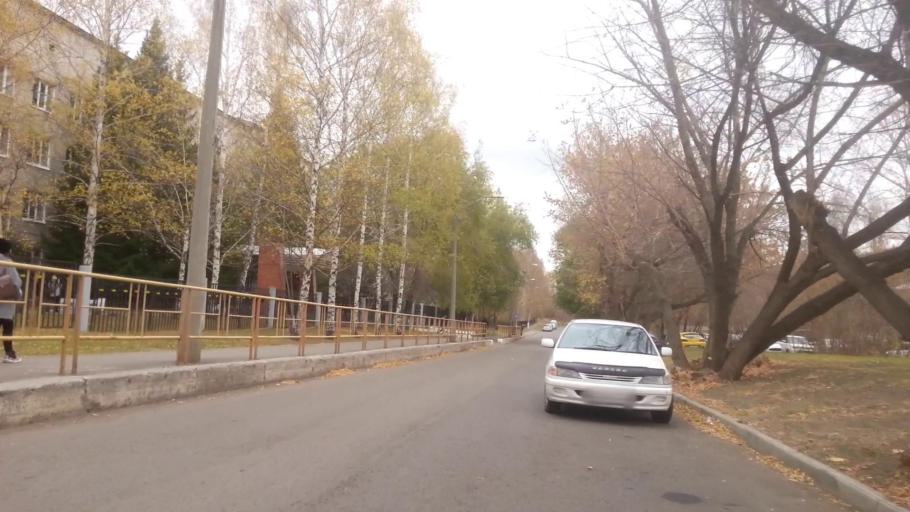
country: RU
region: Altai Krai
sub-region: Gorod Barnaulskiy
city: Barnaul
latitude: 53.3655
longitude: 83.7177
